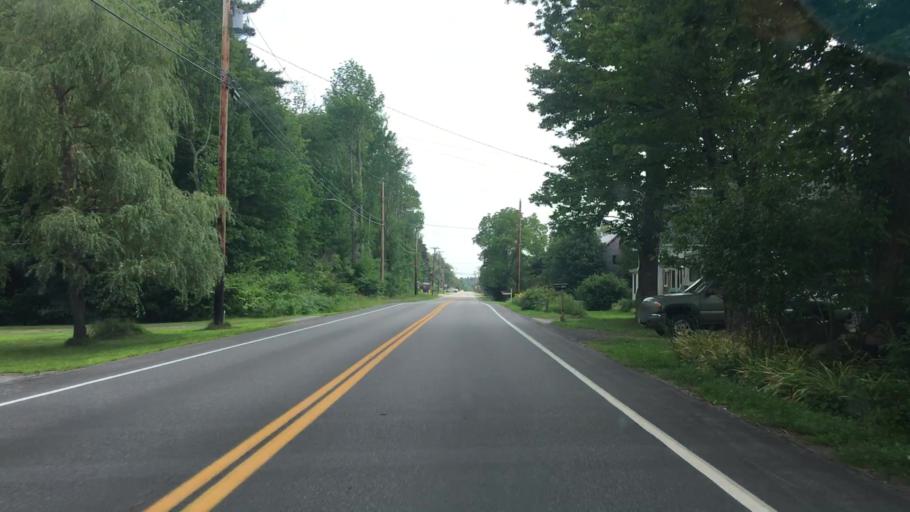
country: US
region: Maine
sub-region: Kennebec County
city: Windsor
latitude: 44.3137
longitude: -69.5818
